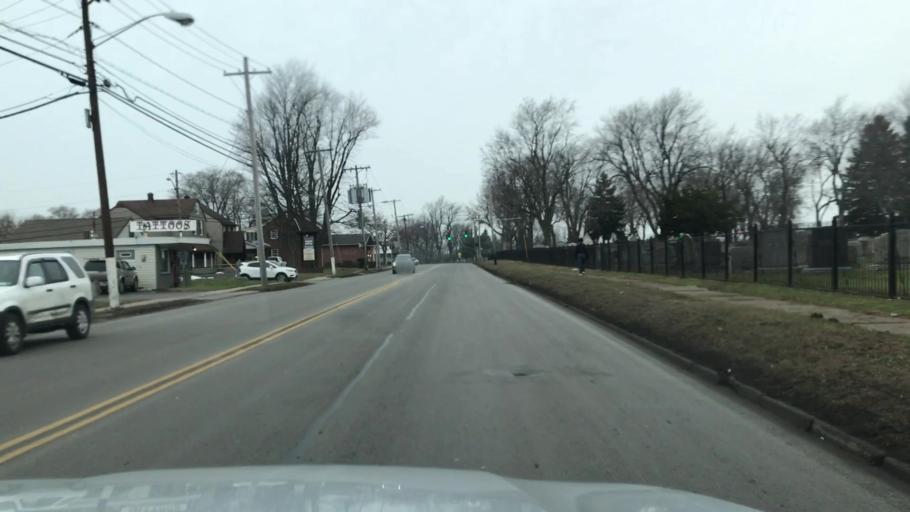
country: US
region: New York
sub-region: Erie County
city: Lackawanna
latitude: 42.8283
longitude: -78.8107
